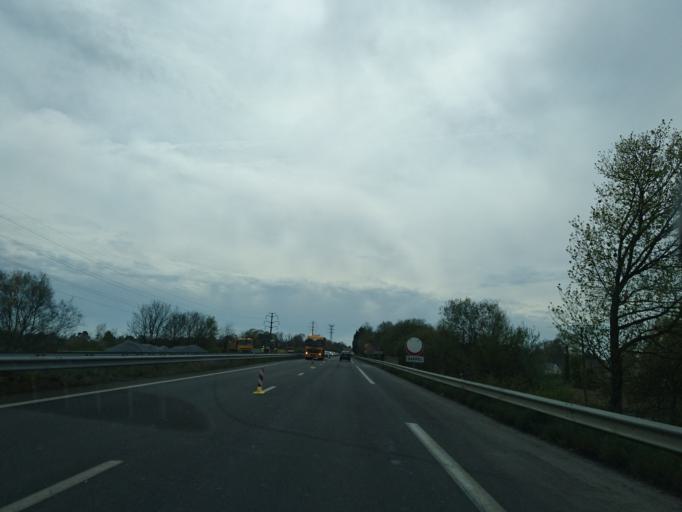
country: FR
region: Brittany
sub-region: Departement des Cotes-d'Armor
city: Quevert
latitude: 48.4622
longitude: -2.0700
